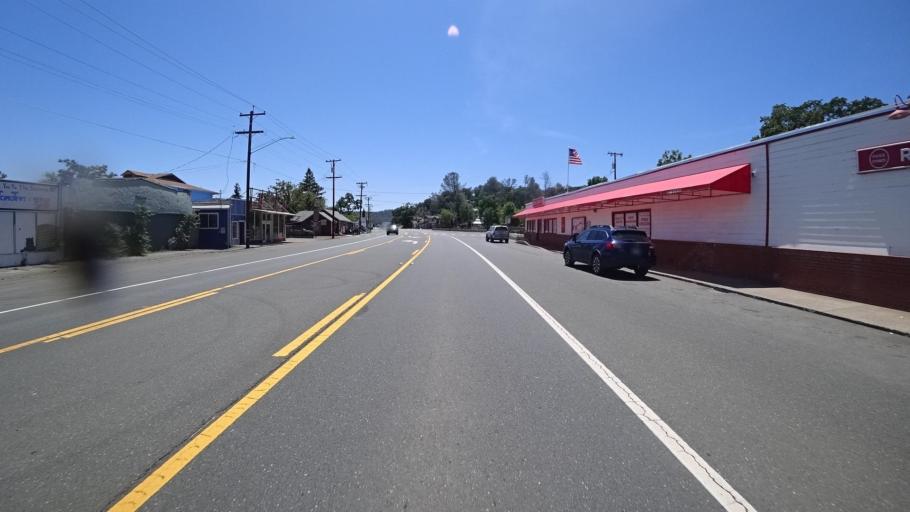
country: US
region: California
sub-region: Lake County
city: Clearlake Oaks
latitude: 39.0240
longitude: -122.6746
